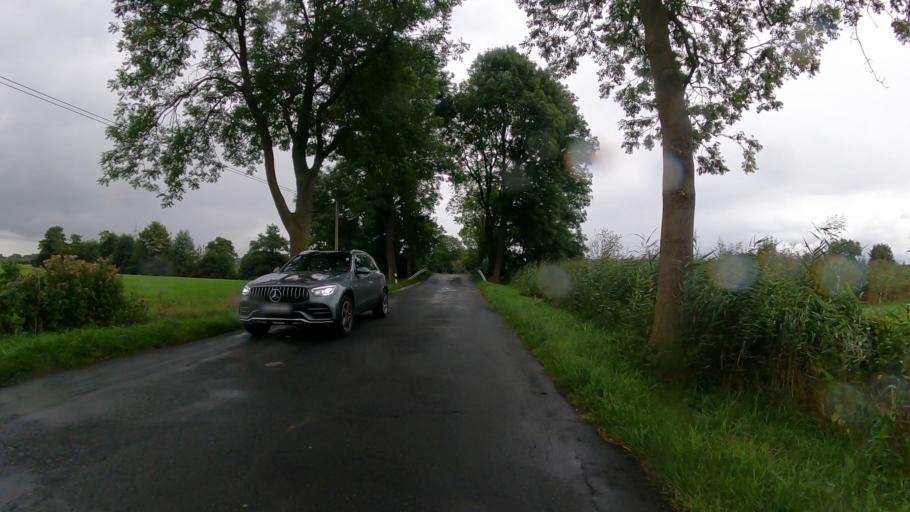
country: DE
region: Lower Saxony
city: Buxtehude
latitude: 53.4831
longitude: 9.7364
